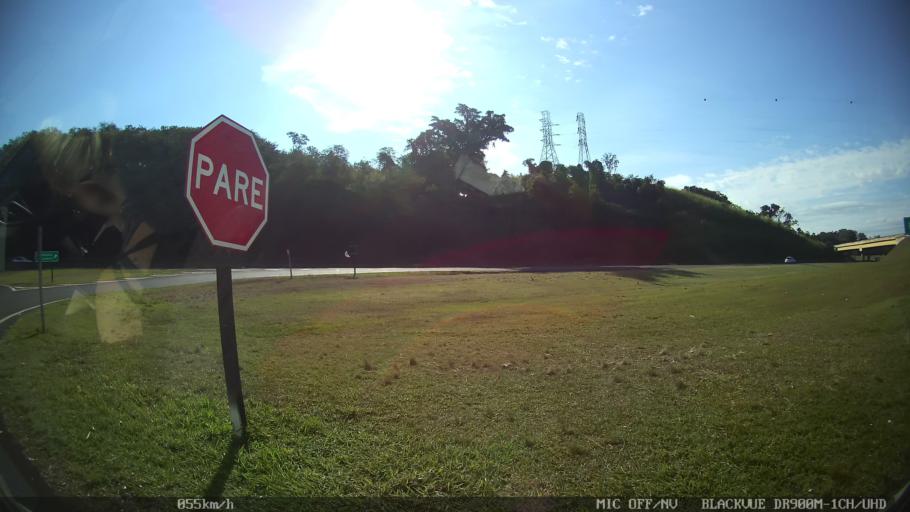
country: BR
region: Sao Paulo
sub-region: Piracicaba
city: Piracicaba
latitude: -22.6881
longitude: -47.5833
